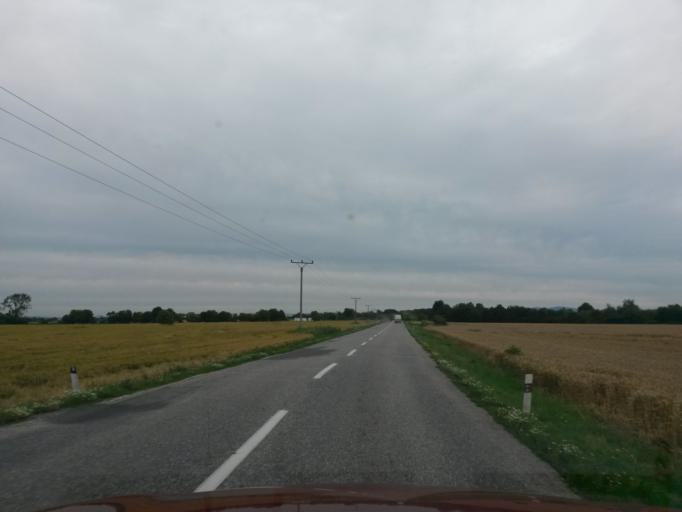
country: SK
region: Nitriansky
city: Levice
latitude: 48.1312
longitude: 18.5941
